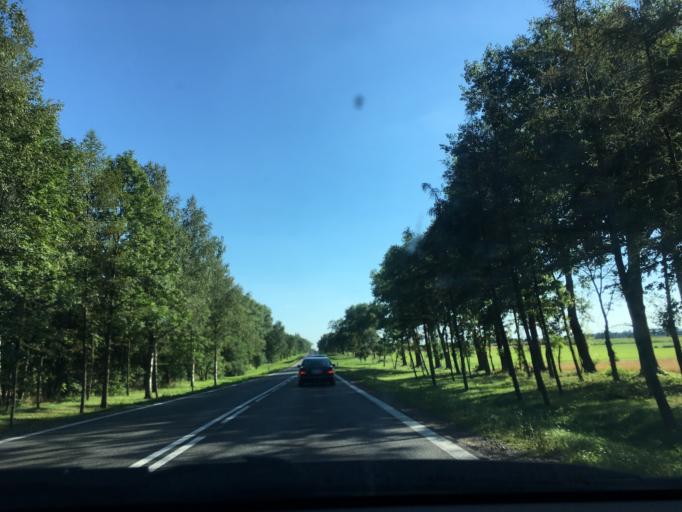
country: PL
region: Podlasie
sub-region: Powiat sokolski
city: Suchowola
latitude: 53.5267
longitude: 23.1072
